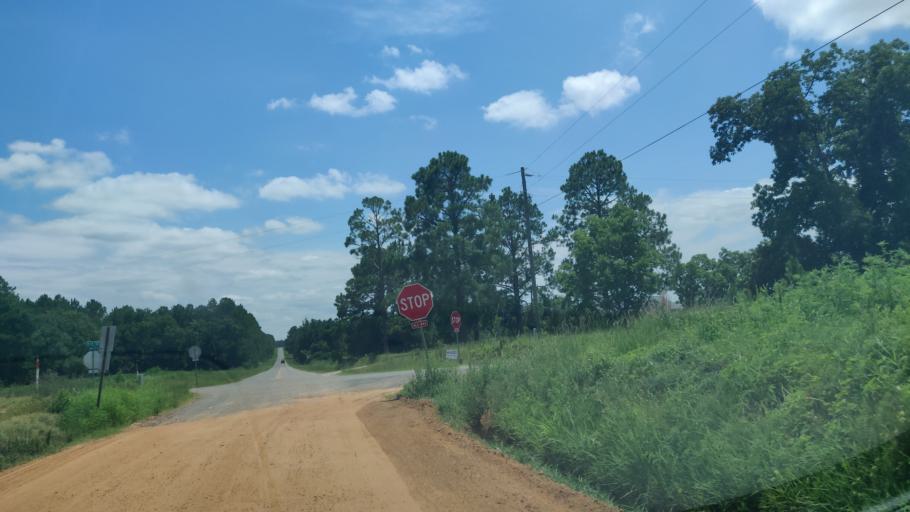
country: US
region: Georgia
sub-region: Tift County
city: Omega
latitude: 31.4607
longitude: -83.6374
